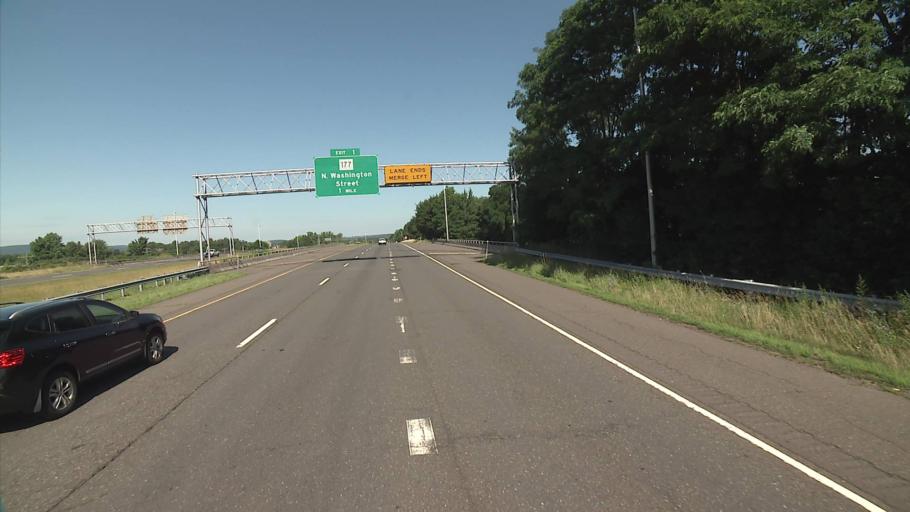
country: US
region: Connecticut
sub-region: Hartford County
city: Plainville
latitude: 41.6756
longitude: -72.8534
